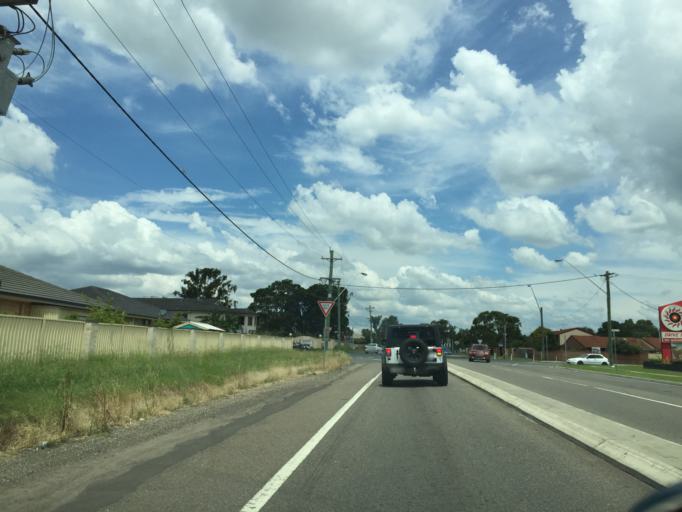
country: AU
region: New South Wales
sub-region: Blacktown
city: Glendenning
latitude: -33.7437
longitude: 150.8429
